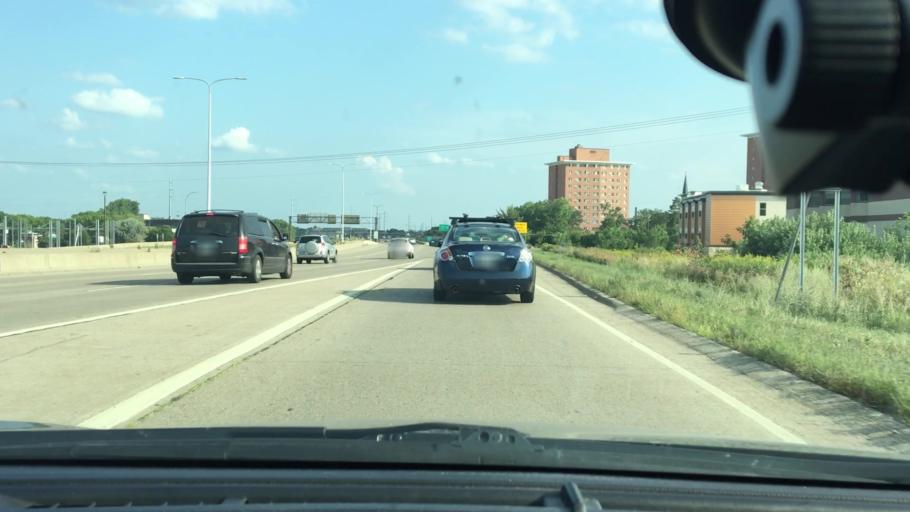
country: US
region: Minnesota
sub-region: Hennepin County
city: Minneapolis
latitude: 44.9642
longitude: -93.2511
